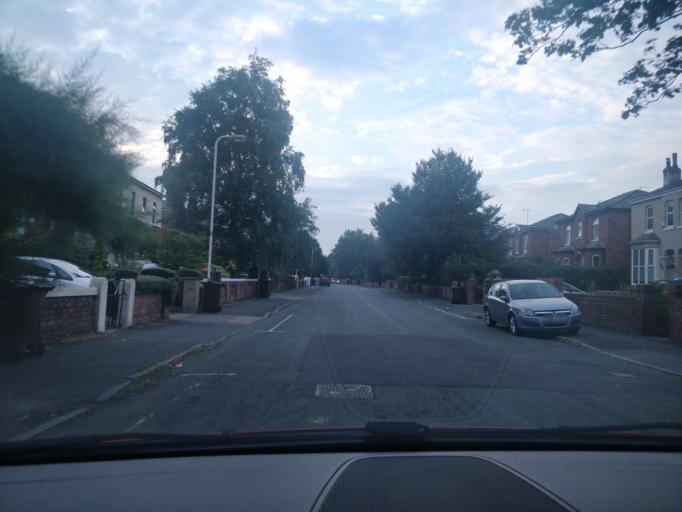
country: GB
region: England
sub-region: Sefton
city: Southport
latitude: 53.6510
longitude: -2.9869
